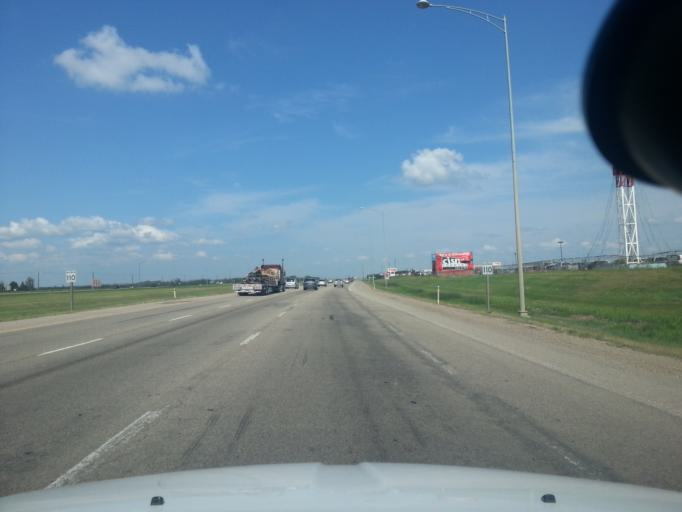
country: CA
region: Alberta
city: Leduc
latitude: 53.3427
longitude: -113.5464
